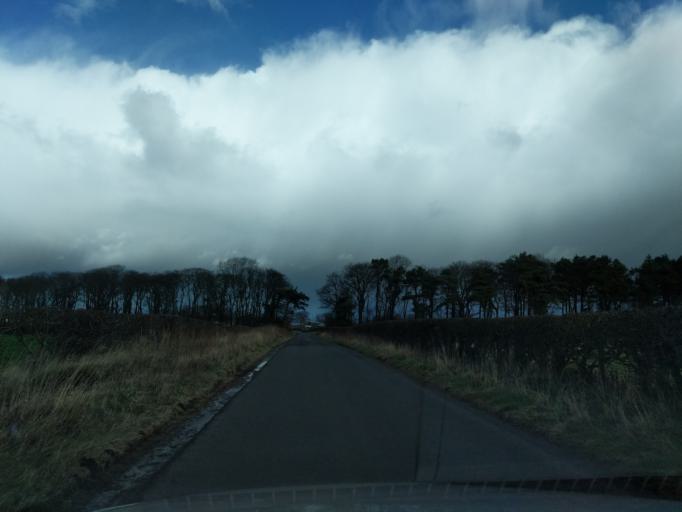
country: GB
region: Scotland
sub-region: Edinburgh
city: Currie
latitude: 55.8808
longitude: -3.3096
